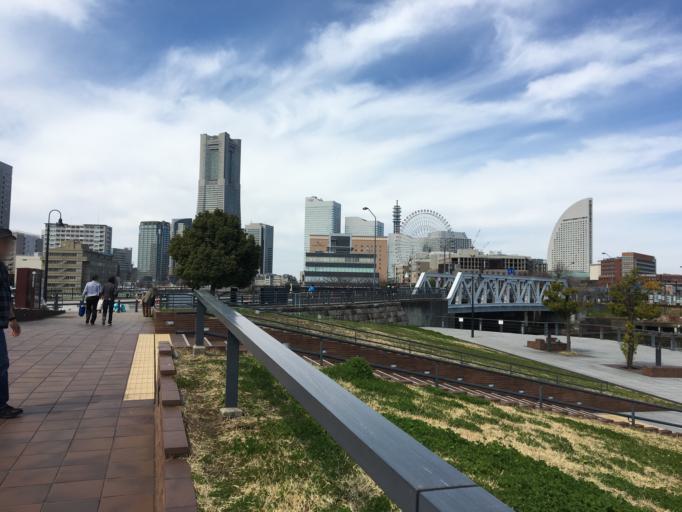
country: JP
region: Kanagawa
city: Yokohama
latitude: 35.4505
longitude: 139.6428
